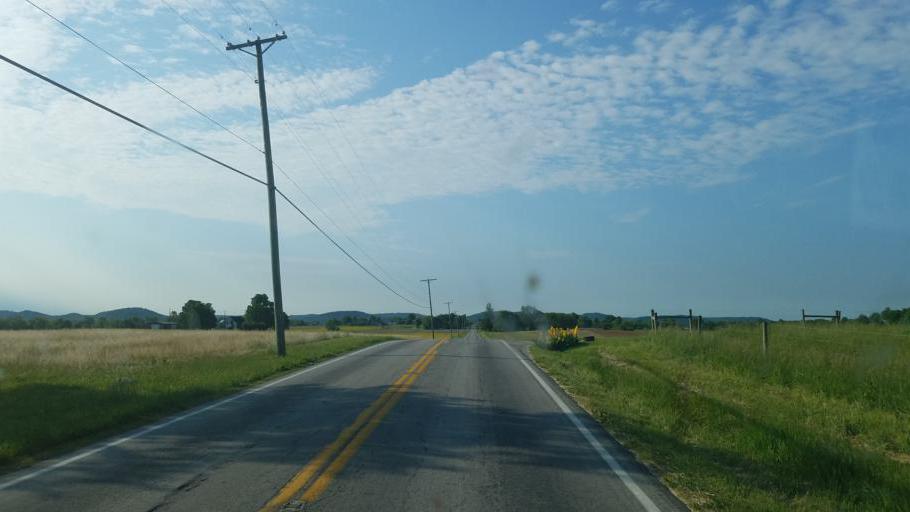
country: US
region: Ohio
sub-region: Highland County
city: Greenfield
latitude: 39.2305
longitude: -83.4269
